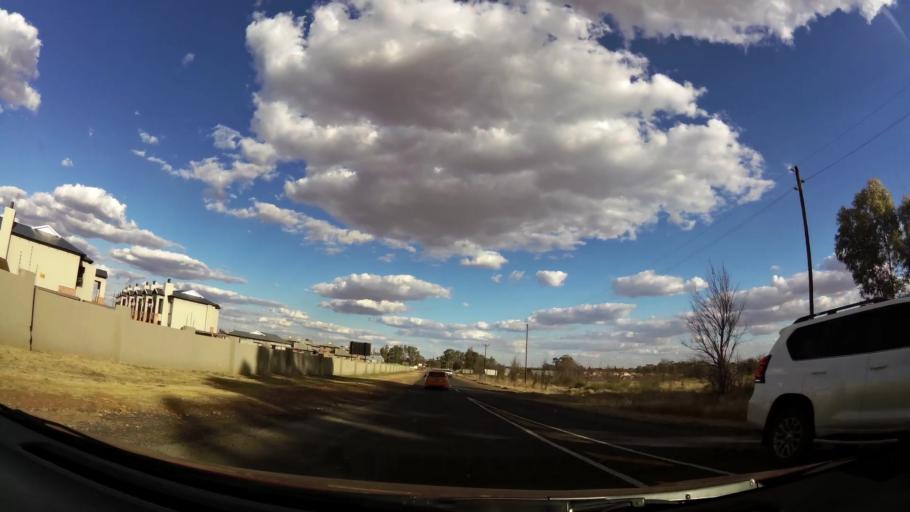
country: ZA
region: North-West
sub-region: Dr Kenneth Kaunda District Municipality
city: Potchefstroom
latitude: -26.6678
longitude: 27.1057
